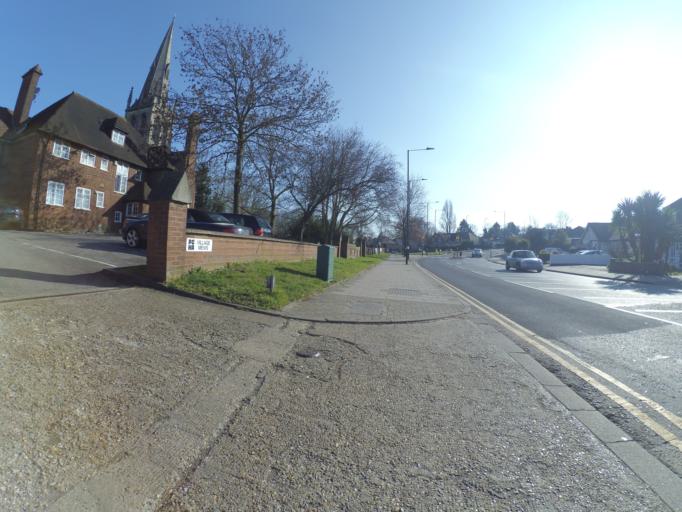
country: GB
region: England
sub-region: Greater London
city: Wembley
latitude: 51.5683
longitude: -0.2627
